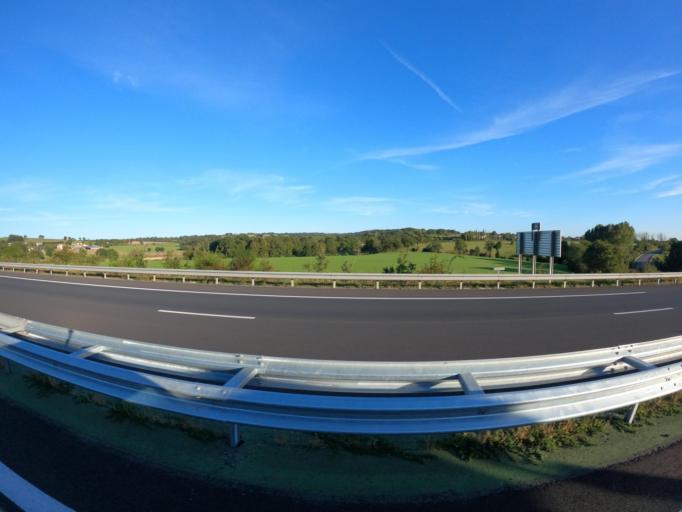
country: FR
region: Pays de la Loire
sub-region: Departement de la Vendee
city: La Gaubretiere
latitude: 46.9120
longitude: -1.0449
